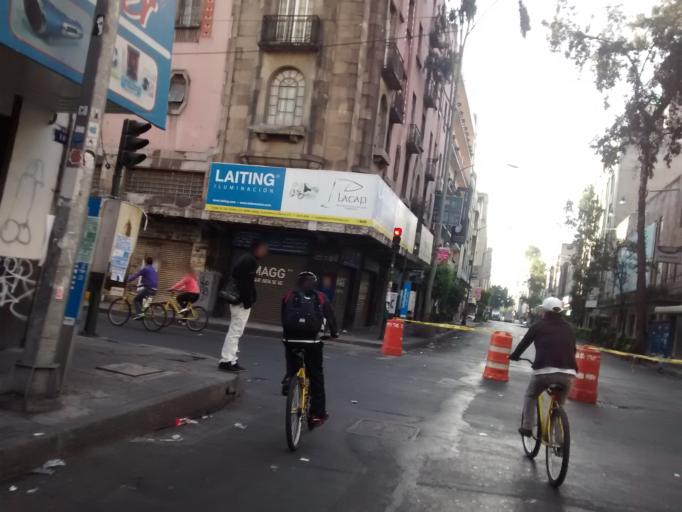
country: MX
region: Mexico City
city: Cuauhtemoc
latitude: 19.4323
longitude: -99.1421
